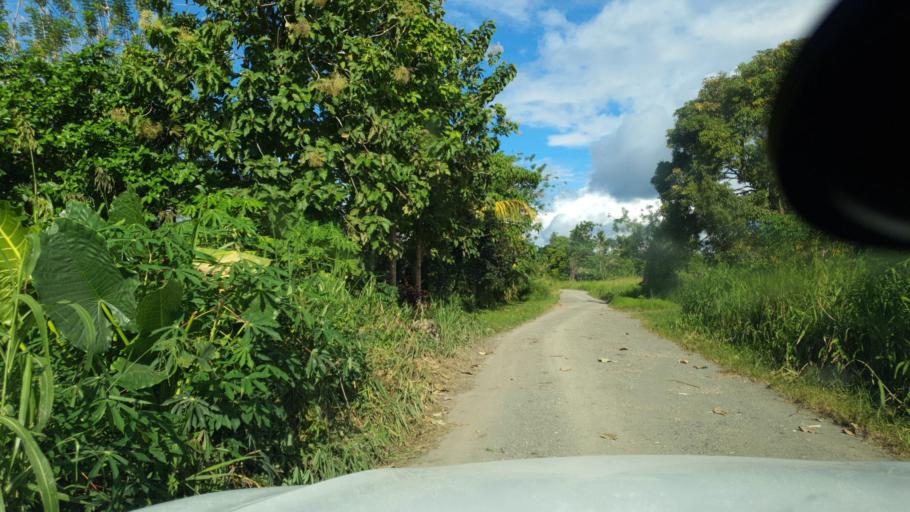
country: SB
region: Guadalcanal
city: Honiara
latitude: -9.4439
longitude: 160.1511
